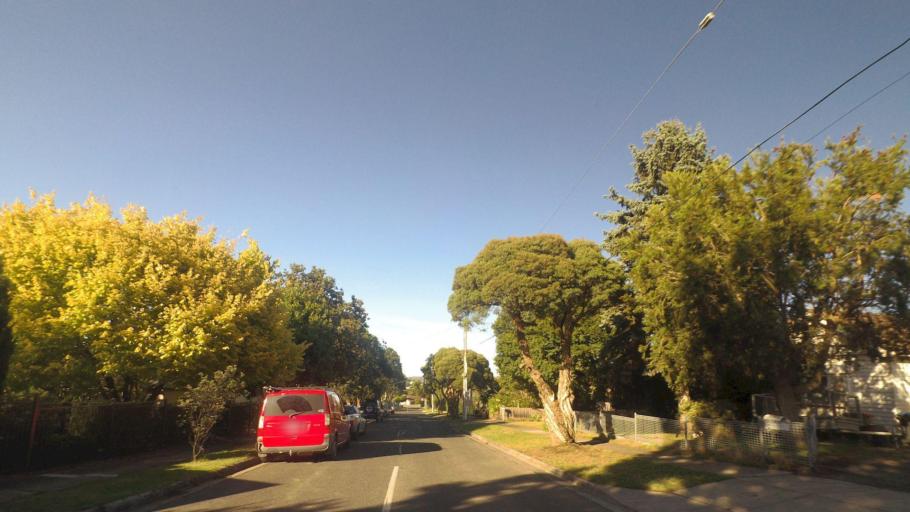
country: AU
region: Victoria
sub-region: Knox
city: Ferntree Gully
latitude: -37.8845
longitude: 145.2917
